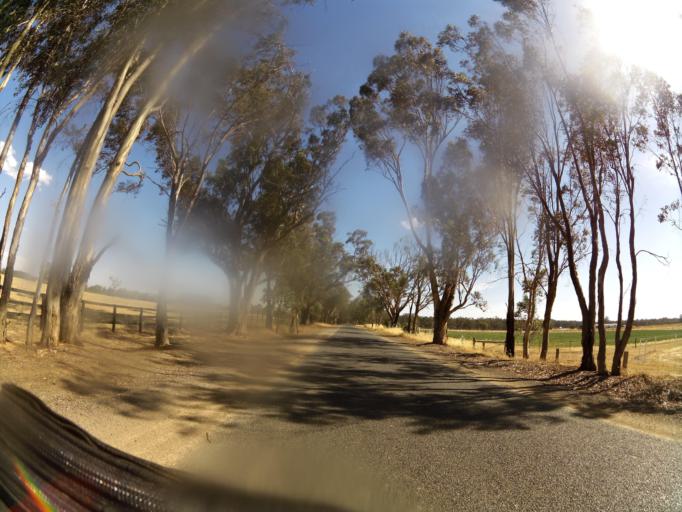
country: AU
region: Victoria
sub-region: Campaspe
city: Kyabram
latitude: -36.8619
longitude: 145.0880
